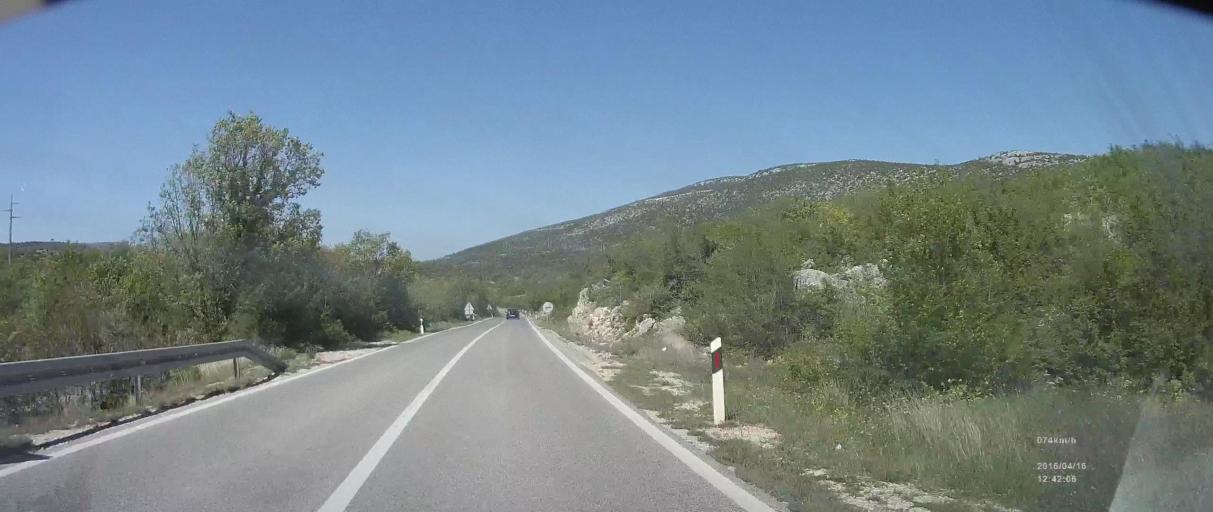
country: HR
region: Sibensko-Kniniska
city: Rogoznica
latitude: 43.6266
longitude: 16.0934
